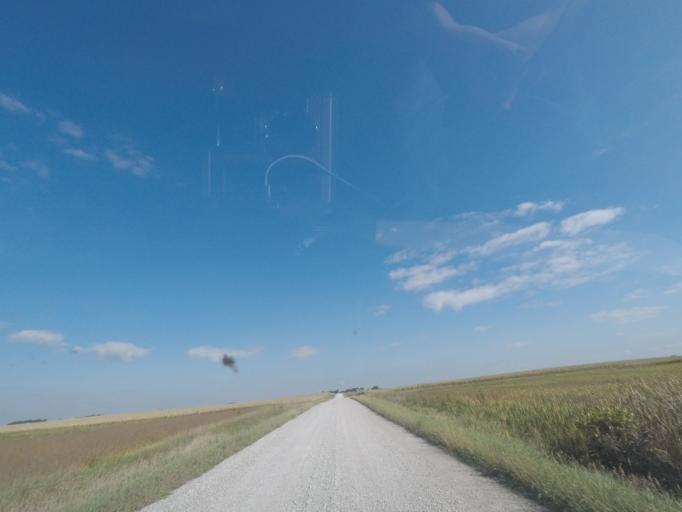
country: US
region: Iowa
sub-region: Story County
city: Nevada
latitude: 42.0478
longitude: -93.4252
